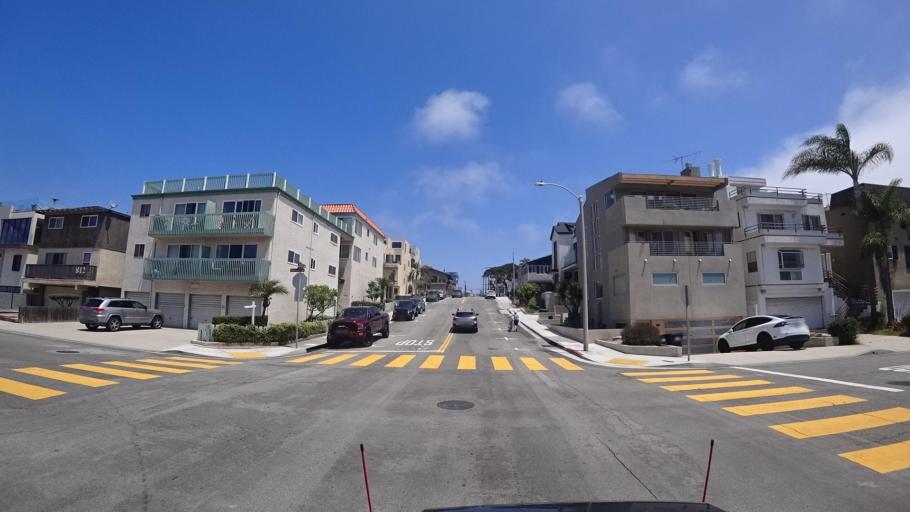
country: US
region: California
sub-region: Los Angeles County
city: Hermosa Beach
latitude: 33.8596
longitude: -118.3974
